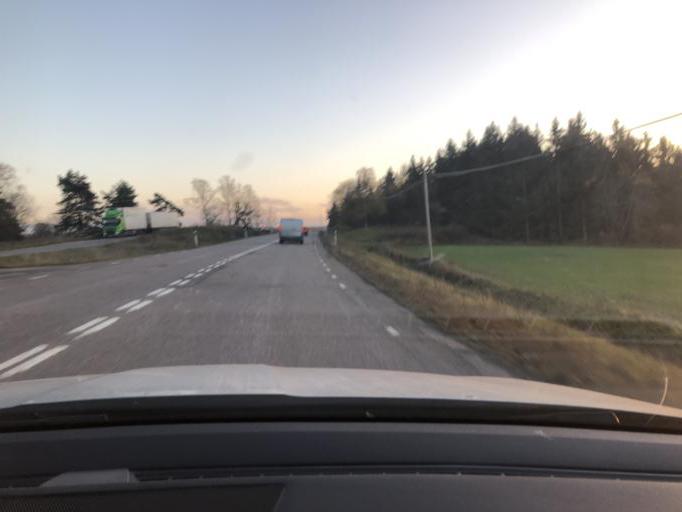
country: SE
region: Soedermanland
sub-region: Strangnas Kommun
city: Akers Styckebruk
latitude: 59.2918
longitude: 17.1080
